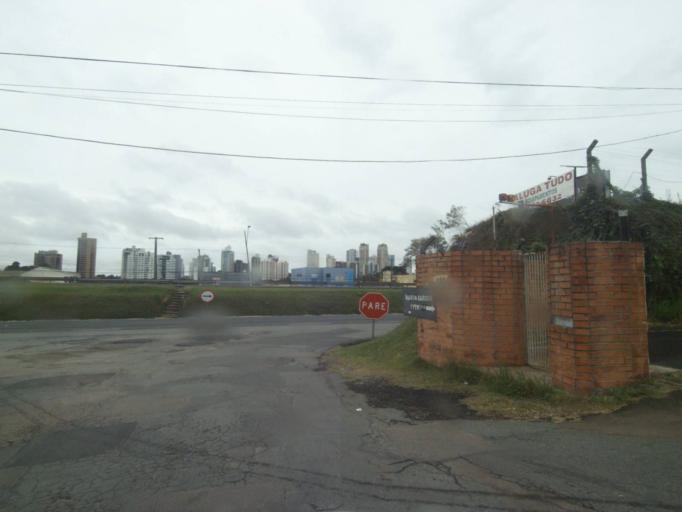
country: BR
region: Parana
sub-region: Curitiba
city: Curitiba
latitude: -25.4303
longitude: -49.3301
